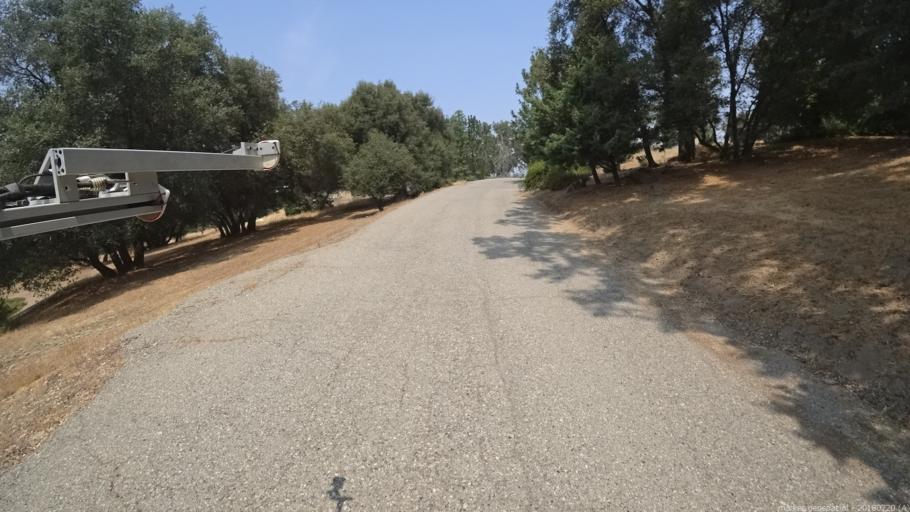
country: US
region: California
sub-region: Madera County
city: Ahwahnee
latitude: 37.3531
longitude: -119.7224
